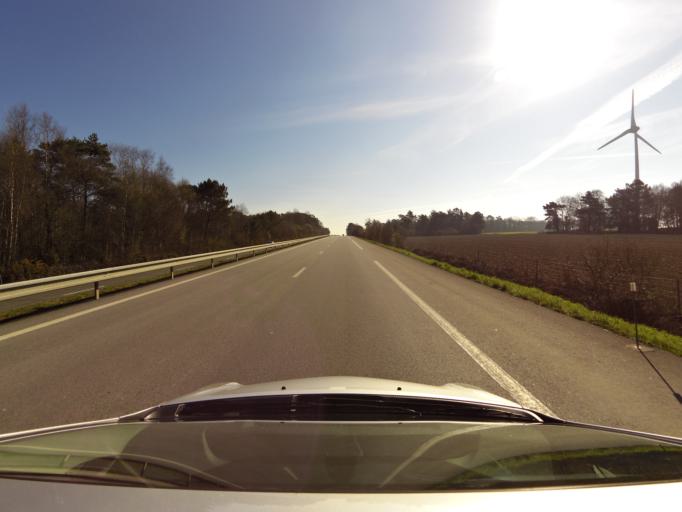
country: FR
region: Brittany
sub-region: Departement du Morbihan
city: Reguiny
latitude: 47.9212
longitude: -2.7073
